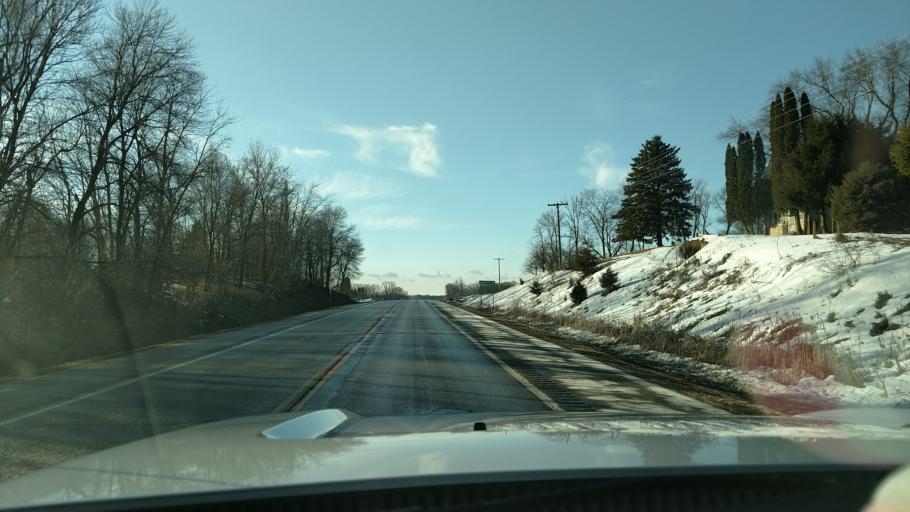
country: US
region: Minnesota
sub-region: Olmsted County
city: Oronoco
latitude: 44.1636
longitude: -92.4191
